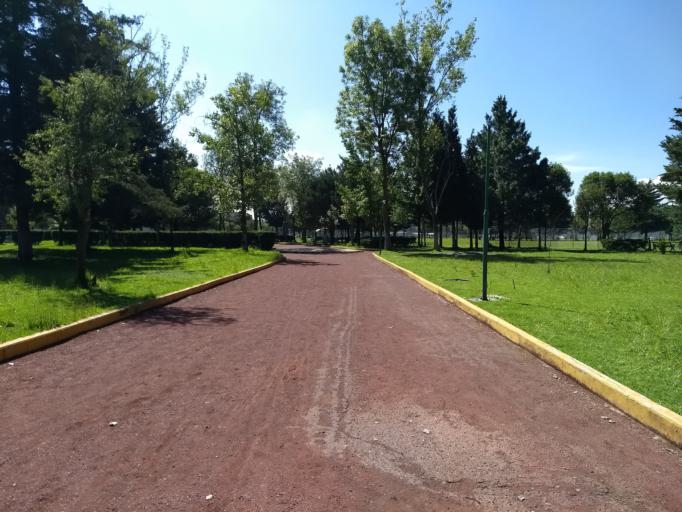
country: MX
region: Mexico
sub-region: Metepec
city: San Salvador Tizatlalli
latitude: 19.2603
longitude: -99.5875
